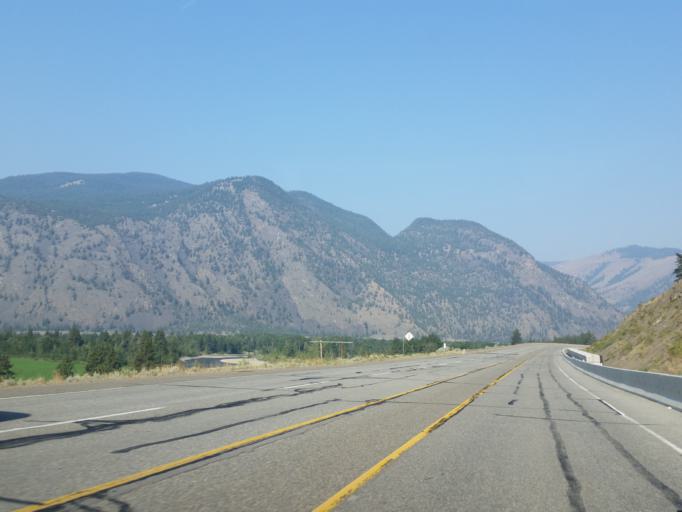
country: CA
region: British Columbia
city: Oliver
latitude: 49.2257
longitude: -119.9621
